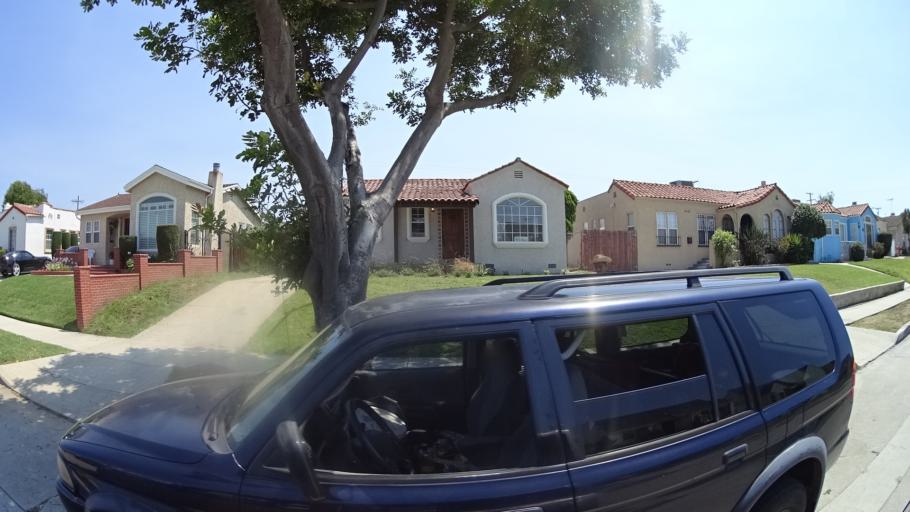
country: US
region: California
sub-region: Los Angeles County
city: Westmont
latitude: 33.9718
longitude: -118.3148
